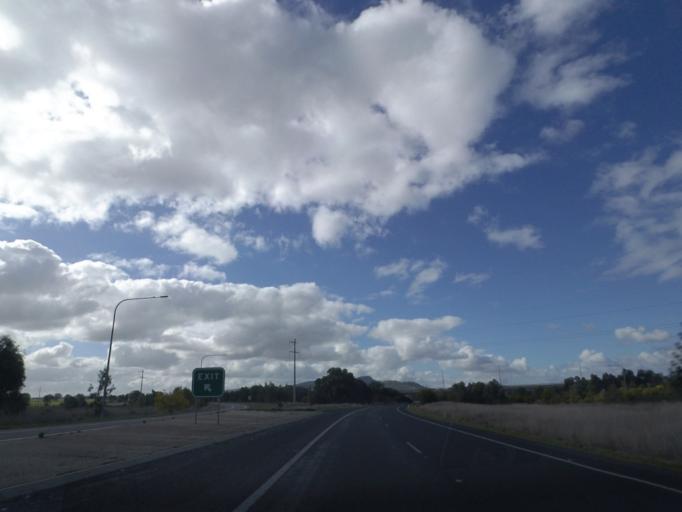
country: AU
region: New South Wales
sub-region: Greater Hume Shire
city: Jindera
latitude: -35.9278
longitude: 147.0044
